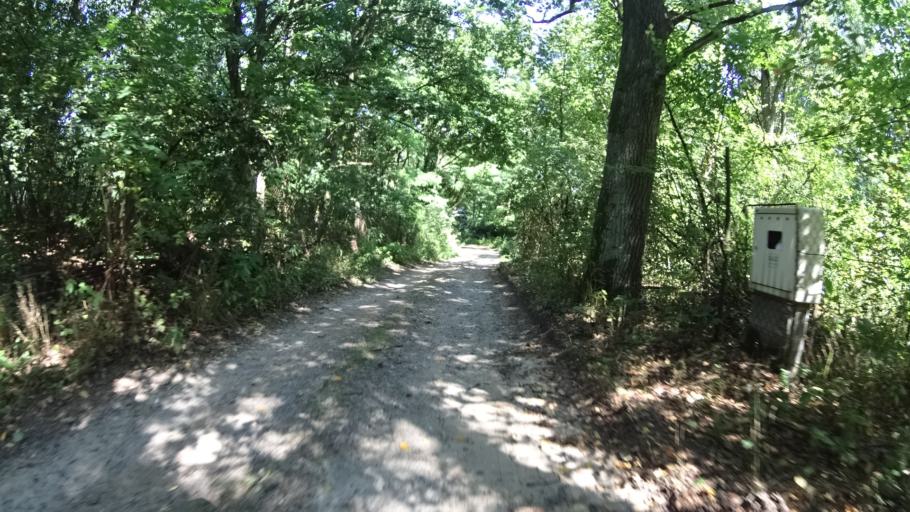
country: PL
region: Masovian Voivodeship
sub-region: Powiat bialobrzeski
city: Bialobrzegi
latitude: 51.6684
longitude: 20.9264
